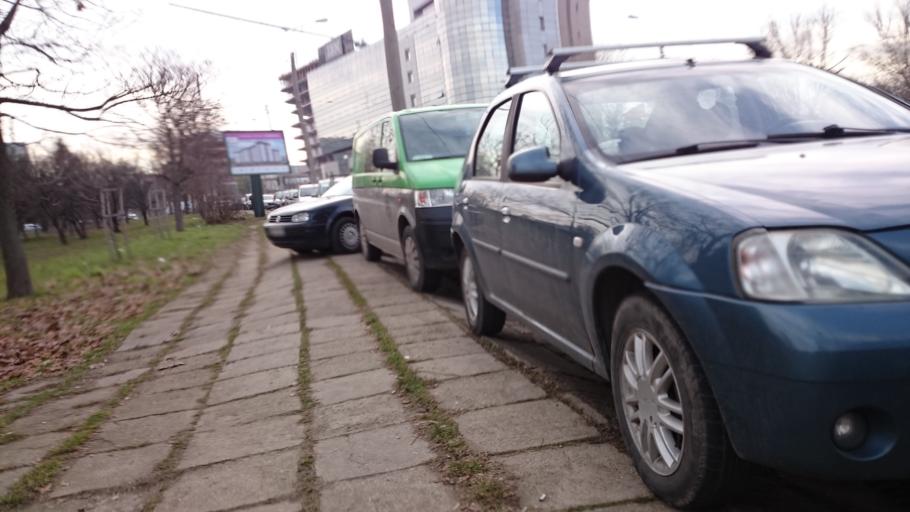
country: RO
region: Bucuresti
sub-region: Municipiul Bucuresti
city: Bucuresti
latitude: 44.4369
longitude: 26.0550
